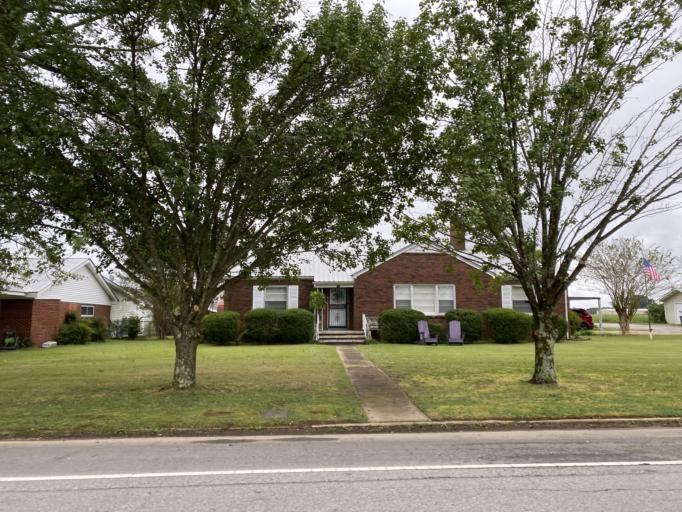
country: US
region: Alabama
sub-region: Franklin County
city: Red Bay
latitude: 34.4427
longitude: -88.1537
